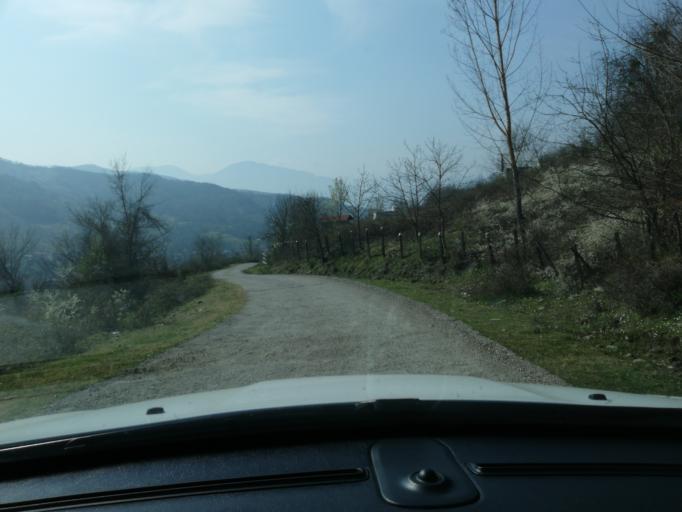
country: TR
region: Karabuk
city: Yenice
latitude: 41.2663
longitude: 32.3599
